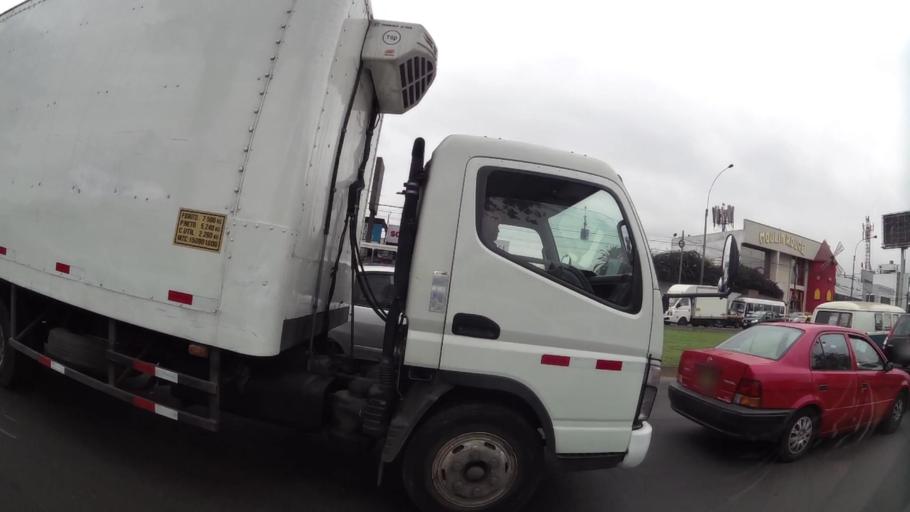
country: PE
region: Lima
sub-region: Lima
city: La Molina
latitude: -12.0787
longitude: -76.9653
